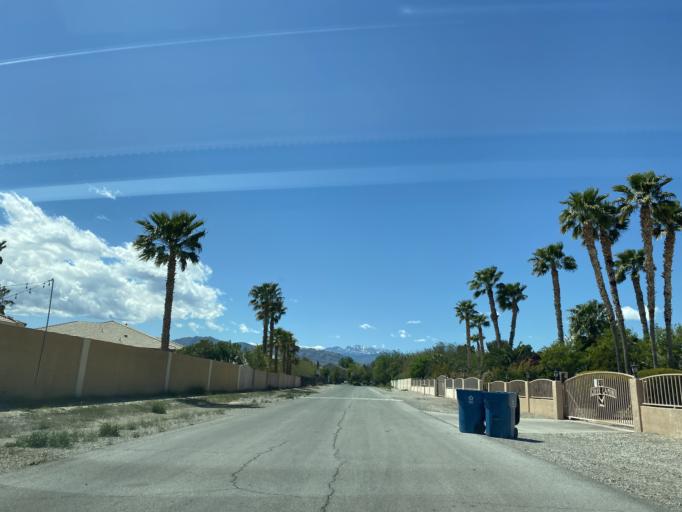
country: US
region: Nevada
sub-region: Clark County
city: North Las Vegas
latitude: 36.2997
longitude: -115.2490
